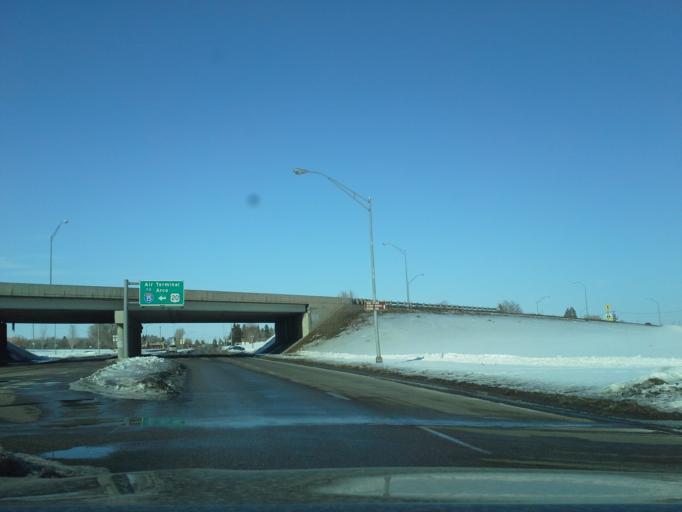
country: US
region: Idaho
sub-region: Bonneville County
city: Idaho Falls
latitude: 43.5078
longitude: -112.0468
